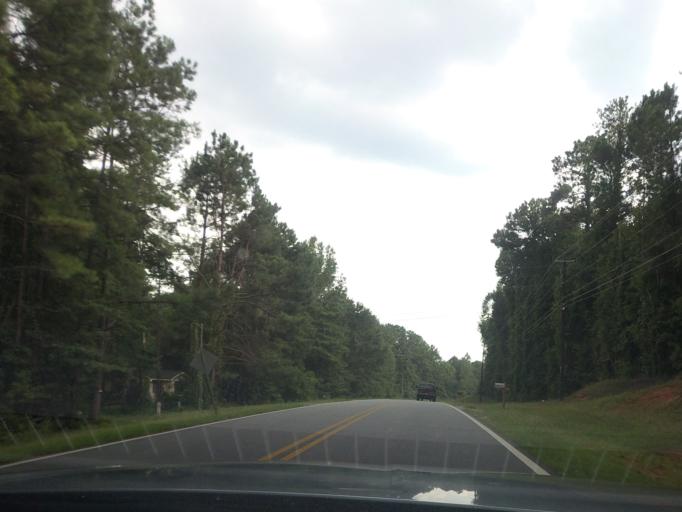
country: US
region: Georgia
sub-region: Bibb County
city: West Point
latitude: 32.8777
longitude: -83.7805
